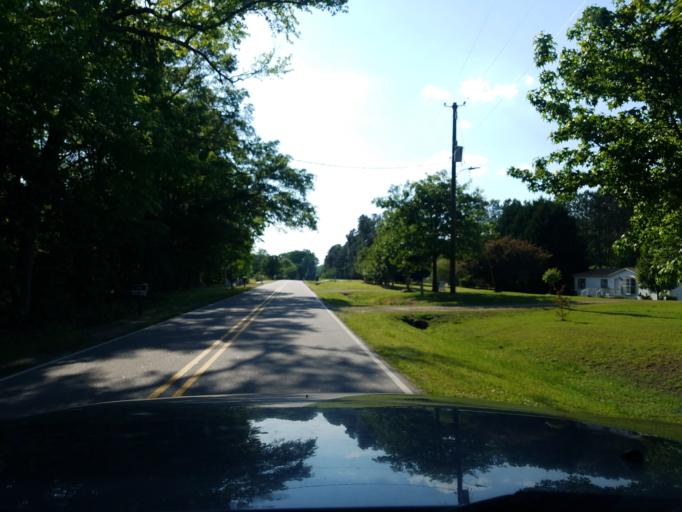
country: US
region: North Carolina
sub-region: Vance County
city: Henderson
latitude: 36.4071
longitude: -78.3720
